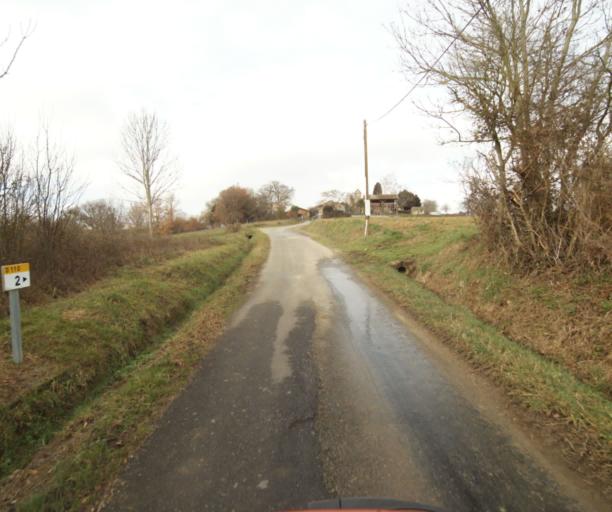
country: FR
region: Midi-Pyrenees
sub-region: Departement de l'Ariege
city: Pamiers
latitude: 43.1050
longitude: 1.5181
